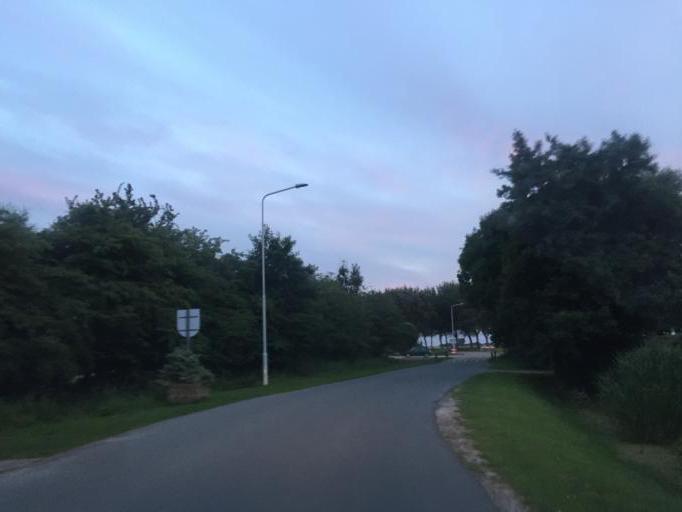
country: NL
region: Friesland
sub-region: Gemeente Dongeradeel
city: Anjum
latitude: 53.4012
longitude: 6.0867
